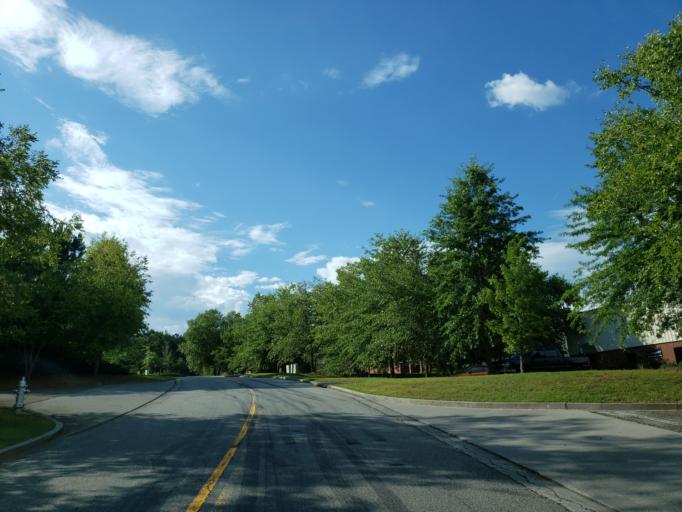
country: US
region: Georgia
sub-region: Cherokee County
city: Ball Ground
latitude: 34.3063
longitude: -84.4213
